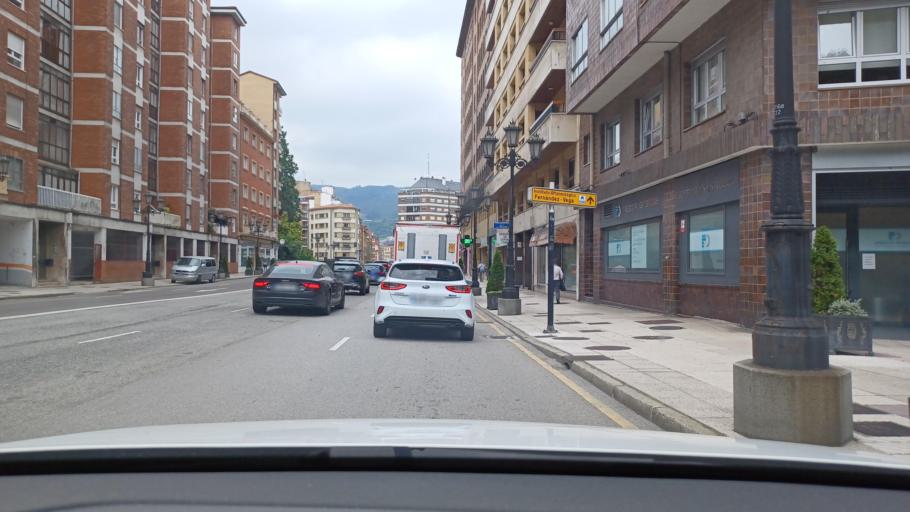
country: ES
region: Asturias
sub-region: Province of Asturias
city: Oviedo
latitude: 43.3599
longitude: -5.8585
